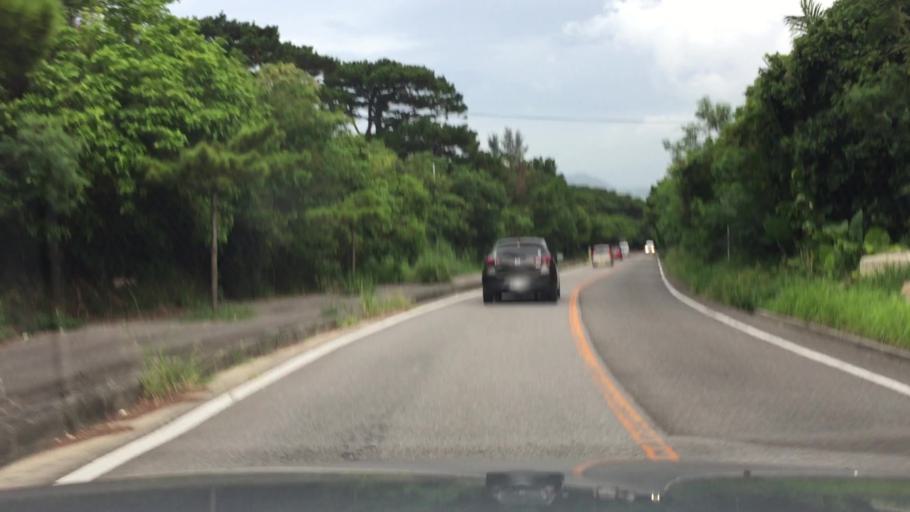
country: JP
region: Okinawa
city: Ishigaki
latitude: 24.4386
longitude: 124.1191
